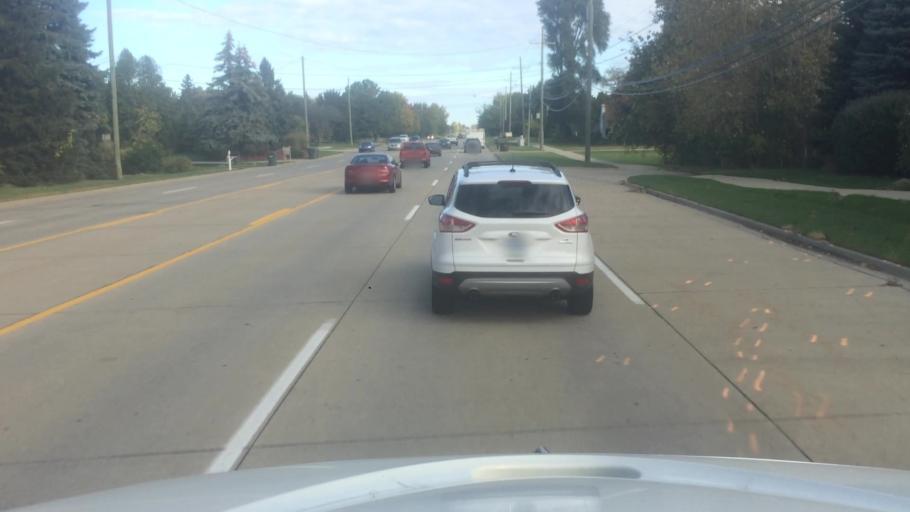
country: US
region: Michigan
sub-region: Macomb County
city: Shelby
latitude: 42.6582
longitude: -82.9941
